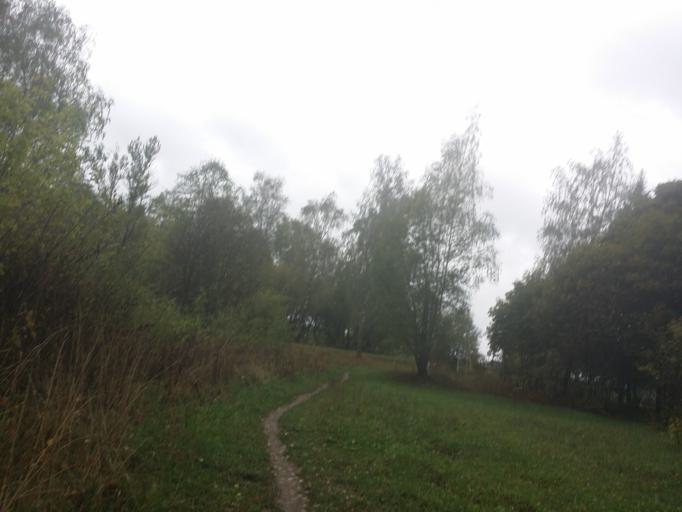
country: BY
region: Minsk
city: Chervyen'
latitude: 53.7625
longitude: 28.2504
